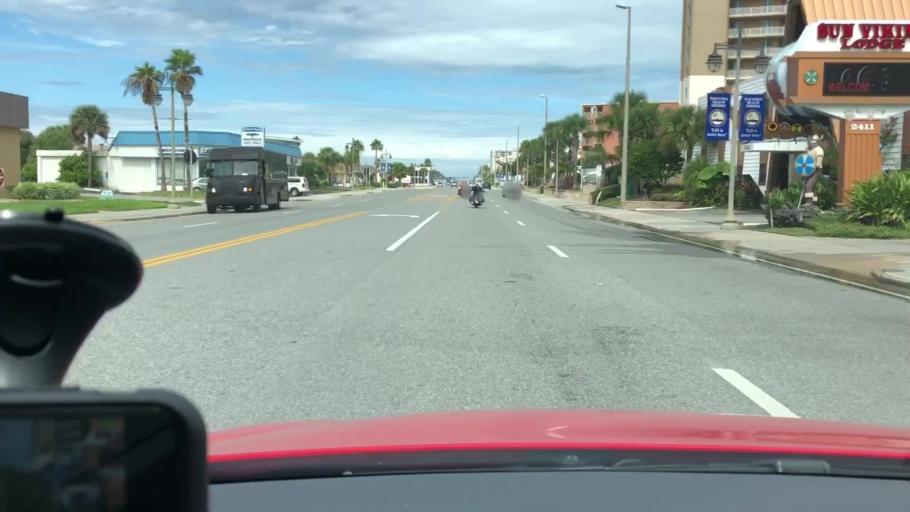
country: US
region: Florida
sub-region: Volusia County
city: Daytona Beach Shores
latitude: 29.1897
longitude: -80.9897
